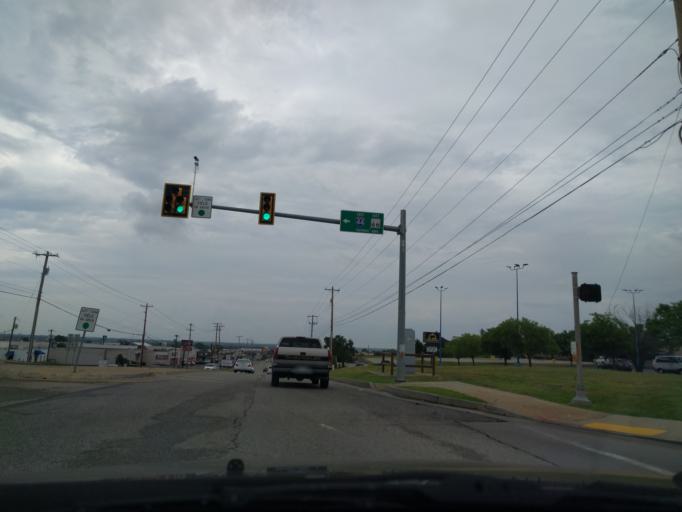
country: US
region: Oklahoma
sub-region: Tulsa County
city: Tulsa
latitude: 36.1043
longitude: -95.9089
